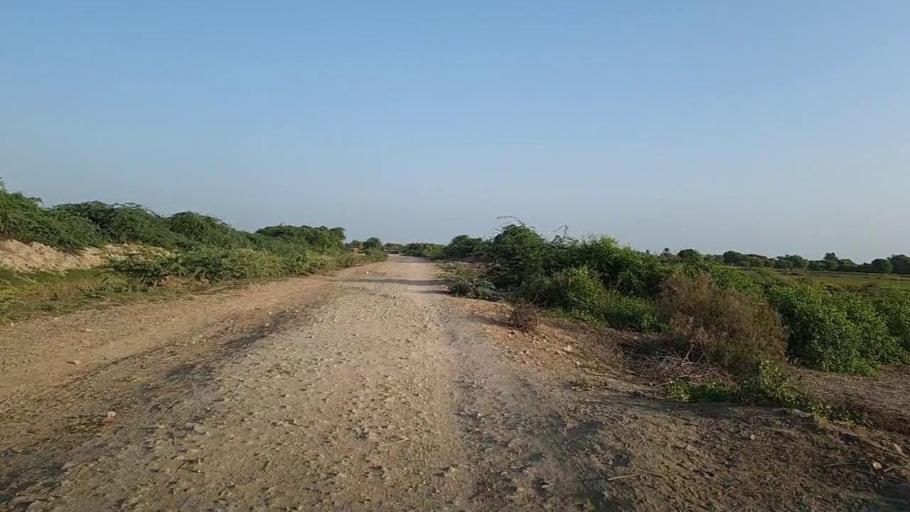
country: PK
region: Sindh
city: Kario
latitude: 24.7046
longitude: 68.6681
